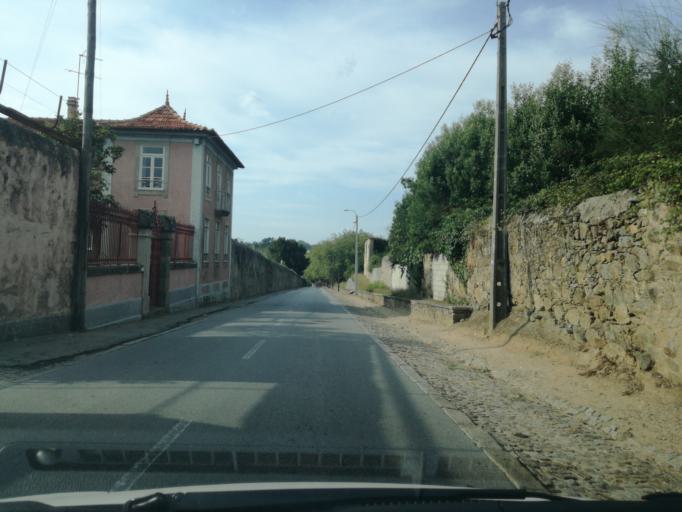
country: PT
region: Porto
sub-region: Vila Nova de Gaia
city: Arcozelo
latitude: 41.0564
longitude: -8.6260
